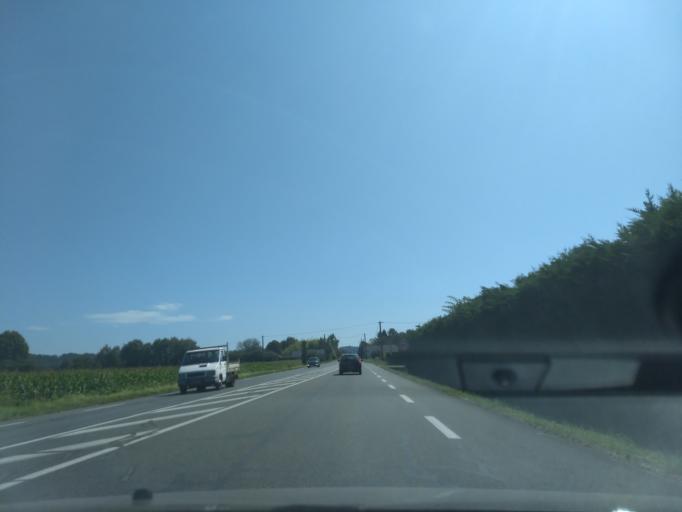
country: FR
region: Aquitaine
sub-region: Departement des Pyrenees-Atlantiques
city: Nousty
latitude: 43.2774
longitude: -0.2275
